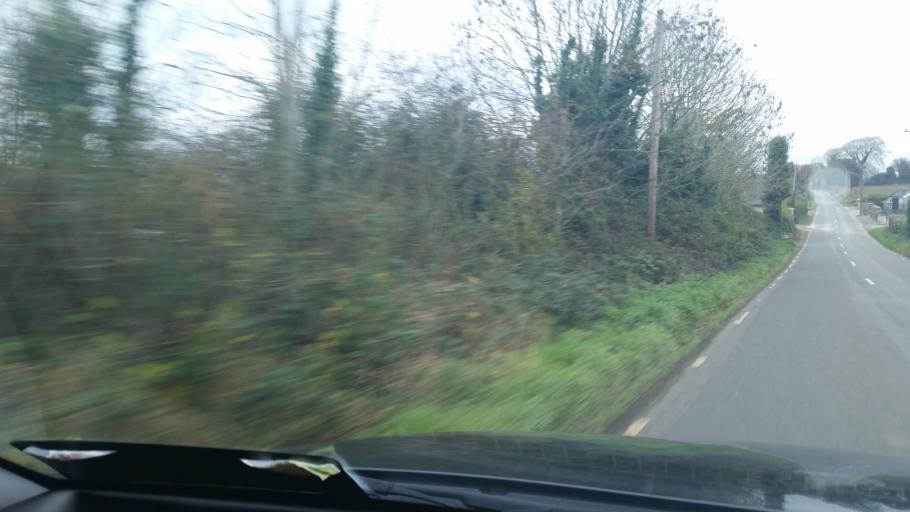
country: IE
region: Leinster
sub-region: Lu
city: Tullyallen
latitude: 53.7019
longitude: -6.4074
